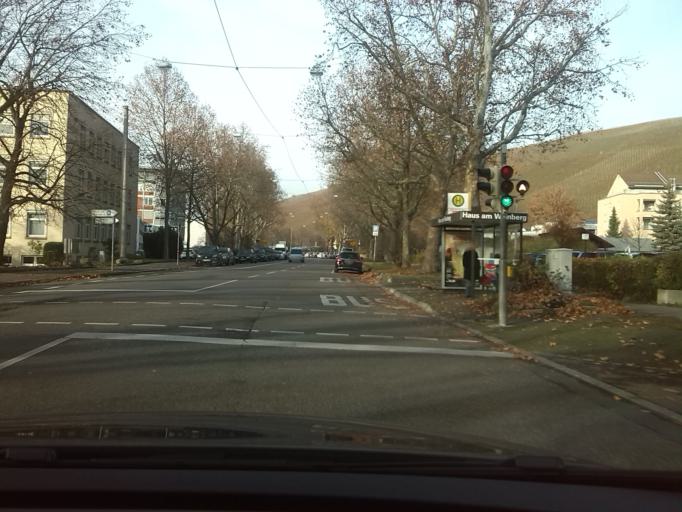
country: DE
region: Baden-Wuerttemberg
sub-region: Regierungsbezirk Stuttgart
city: Fellbach
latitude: 48.7701
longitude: 9.2629
